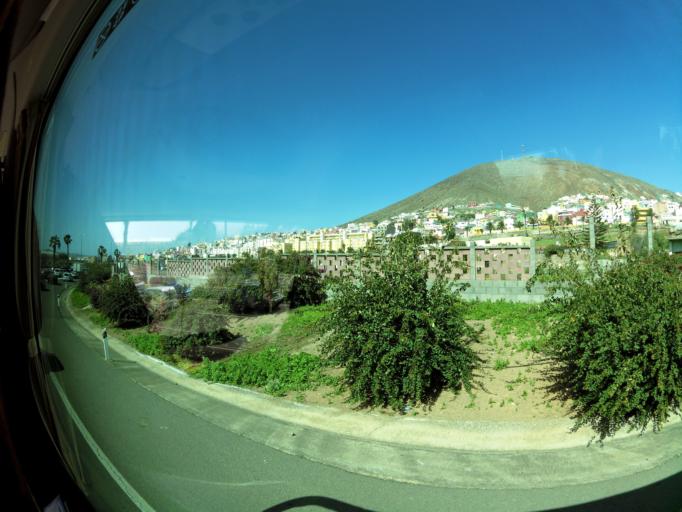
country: ES
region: Canary Islands
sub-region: Provincia de Las Palmas
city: Guia
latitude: 28.1433
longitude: -15.6390
